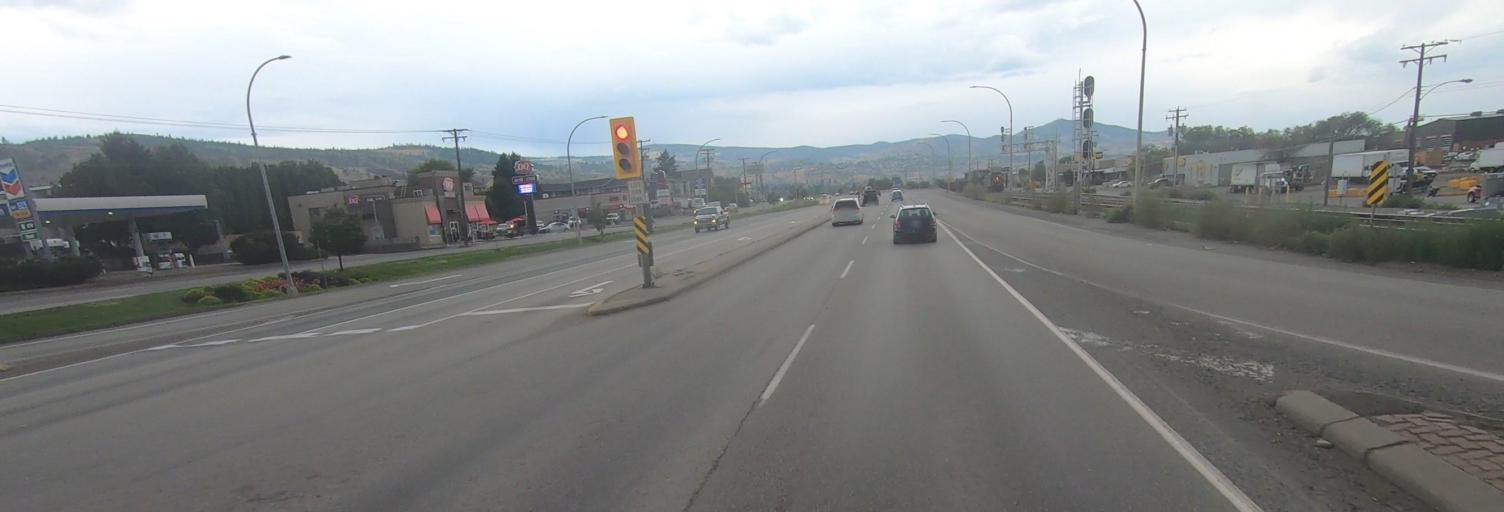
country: CA
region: British Columbia
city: Kamloops
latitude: 50.6786
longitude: -120.2834
